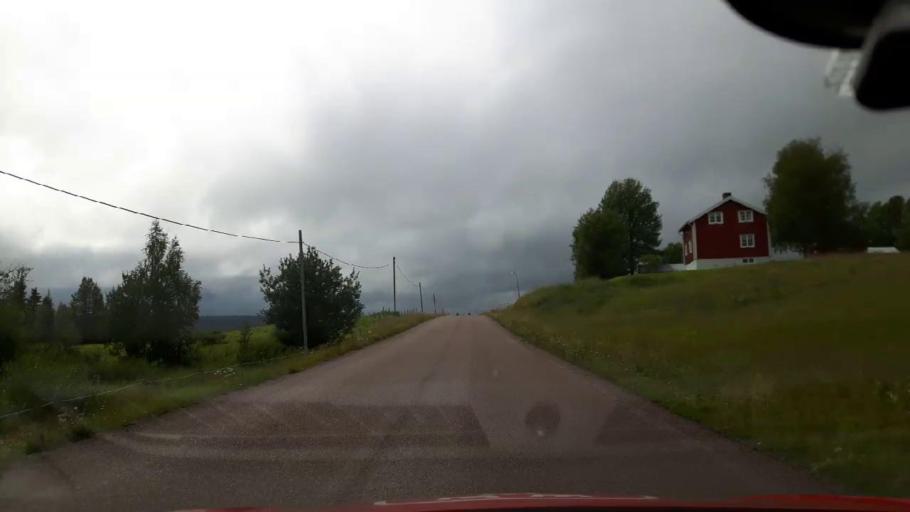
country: SE
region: Jaemtland
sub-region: Krokoms Kommun
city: Valla
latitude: 63.3861
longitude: 13.8181
